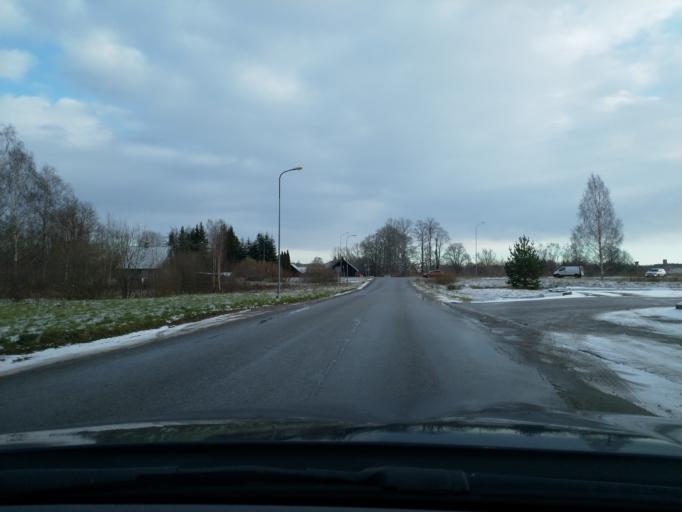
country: LV
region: Kuldigas Rajons
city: Kuldiga
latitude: 56.9594
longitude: 21.9911
